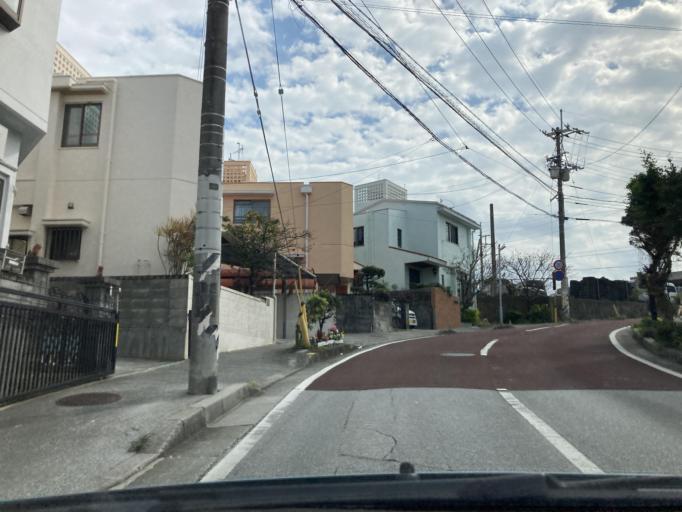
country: JP
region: Okinawa
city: Tomigusuku
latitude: 26.1870
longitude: 127.6961
